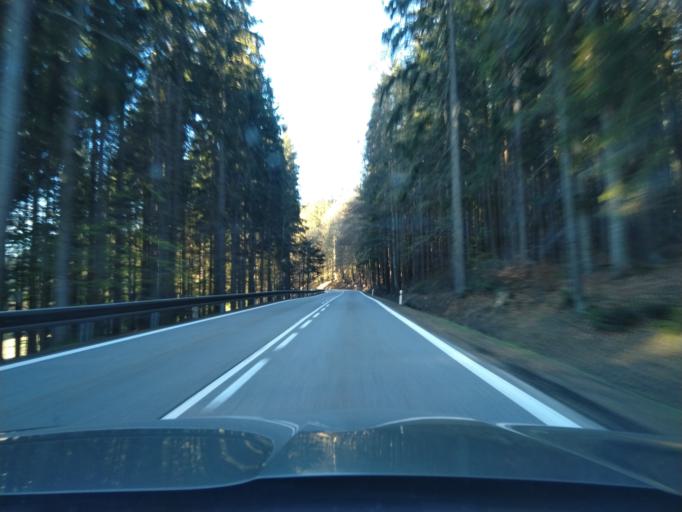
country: CZ
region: Jihocesky
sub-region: Okres Prachatice
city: Vimperk
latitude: 48.9984
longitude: 13.7688
